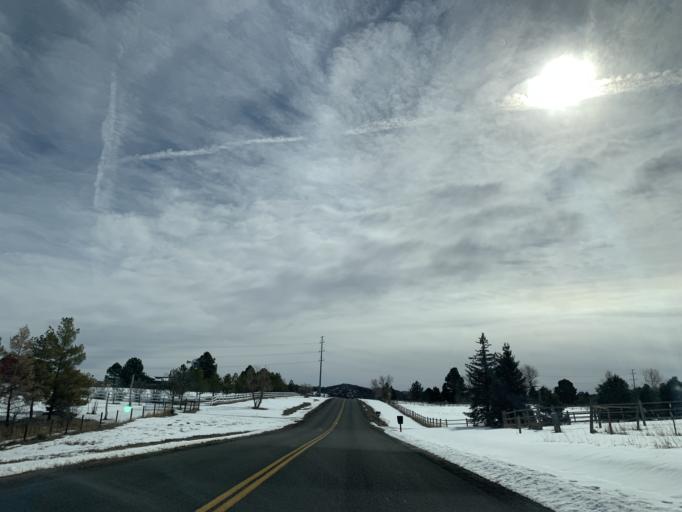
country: US
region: Colorado
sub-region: Douglas County
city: Carriage Club
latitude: 39.5174
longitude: -104.9074
